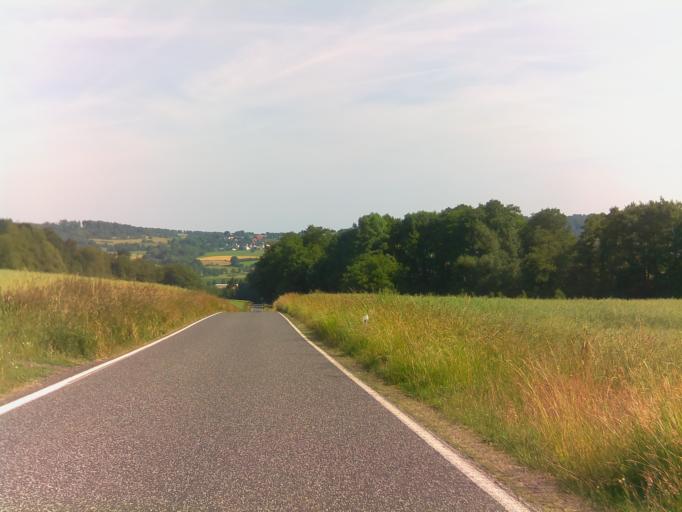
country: DE
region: Hesse
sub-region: Regierungsbezirk Giessen
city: Rabenau
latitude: 50.6650
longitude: 8.8332
